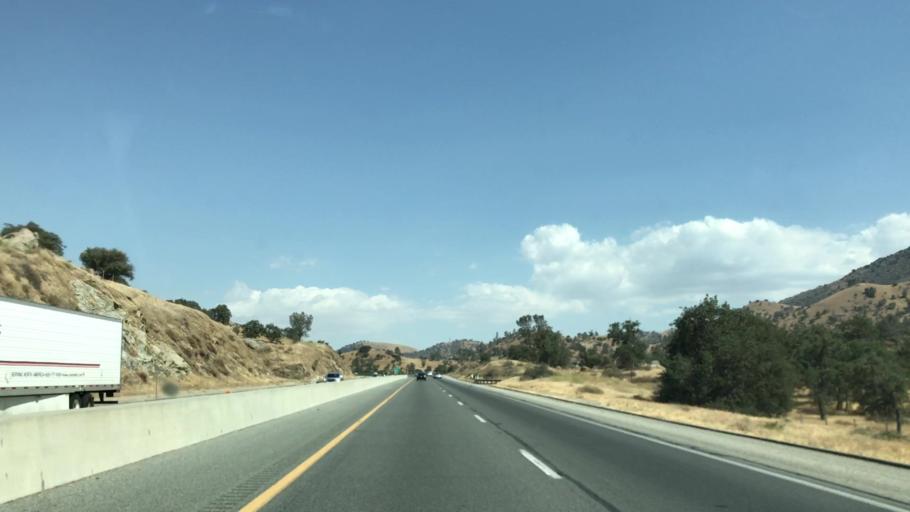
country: US
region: California
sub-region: Kern County
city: Golden Hills
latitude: 35.2059
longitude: -118.5332
